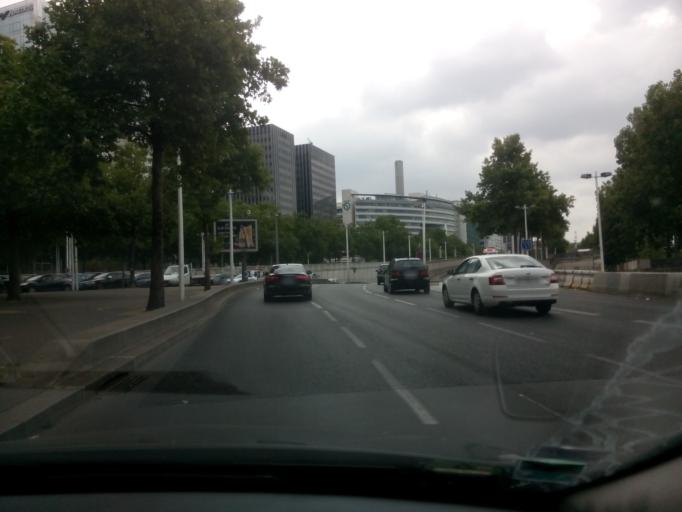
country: FR
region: Ile-de-France
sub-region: Paris
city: Paris
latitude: 48.8442
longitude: 2.3687
